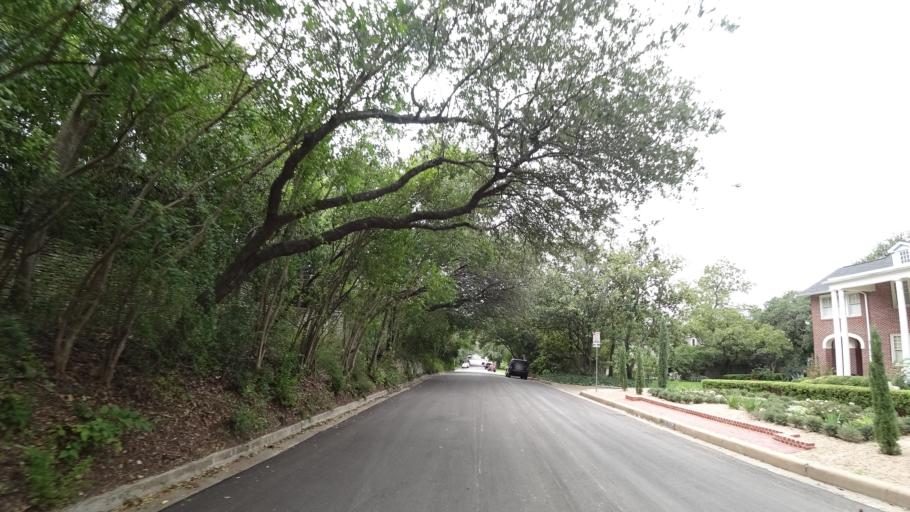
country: US
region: Texas
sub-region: Travis County
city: Austin
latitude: 30.2951
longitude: -97.7259
